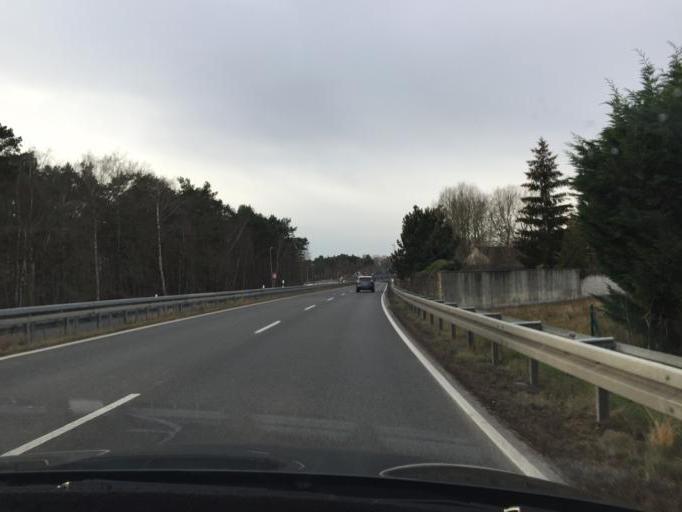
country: DE
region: Brandenburg
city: Peitz
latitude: 51.8085
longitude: 14.3881
